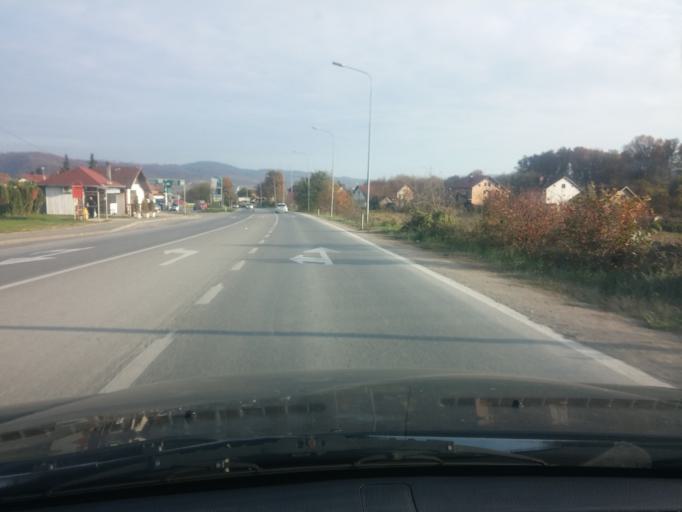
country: BA
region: Republika Srpska
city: Banja Luka
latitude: 44.8224
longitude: 17.1950
